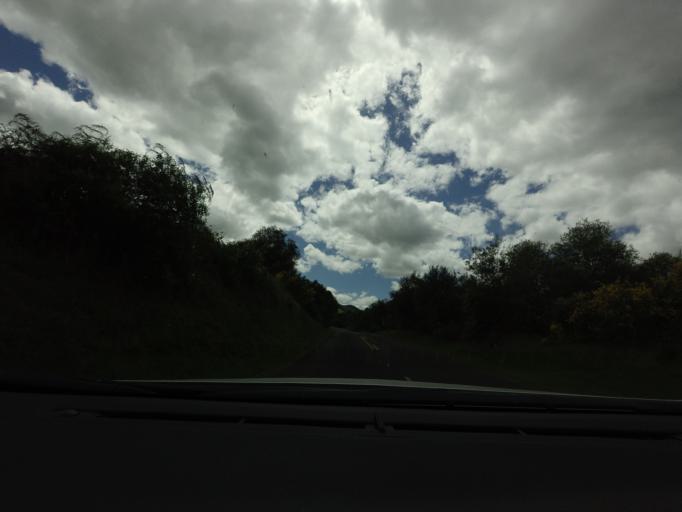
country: NZ
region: Bay of Plenty
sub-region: Rotorua District
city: Rotorua
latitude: -38.3542
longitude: 176.3623
